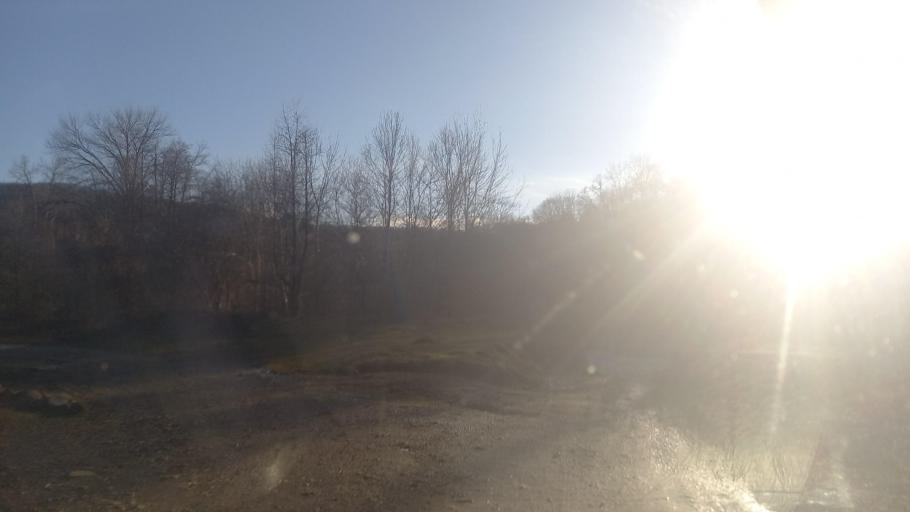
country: RU
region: Krasnodarskiy
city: Smolenskaya
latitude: 44.6150
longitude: 38.7440
